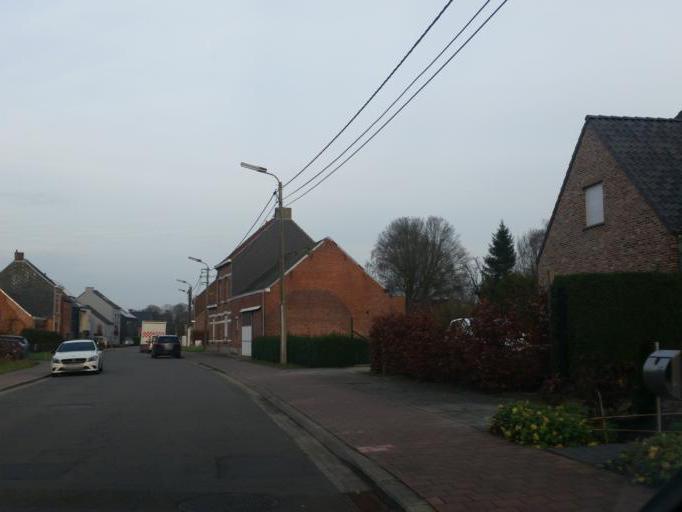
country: BE
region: Flanders
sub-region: Provincie Antwerpen
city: Duffel
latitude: 51.0644
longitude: 4.4928
